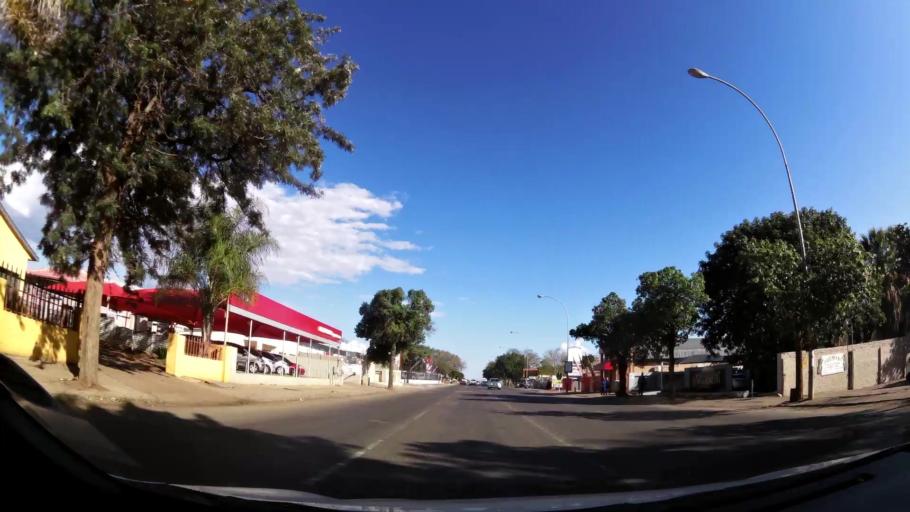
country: ZA
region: Limpopo
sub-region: Waterberg District Municipality
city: Mokopane
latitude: -24.1763
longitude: 29.0156
